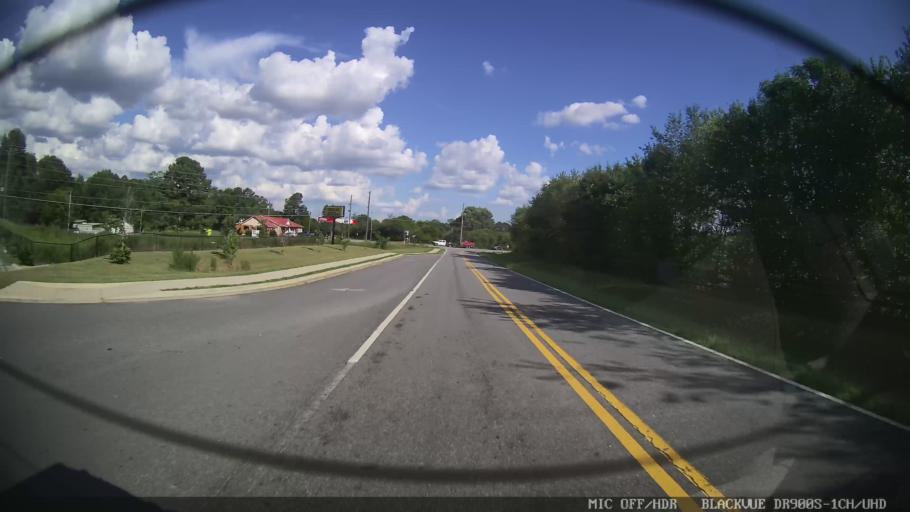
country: US
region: Georgia
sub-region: Bartow County
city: Euharlee
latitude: 34.1448
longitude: -84.9789
